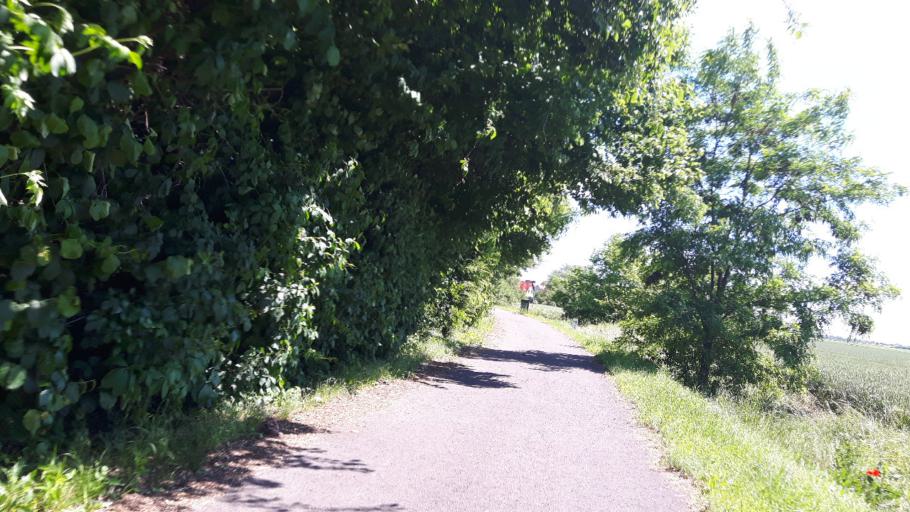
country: DE
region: Saxony-Anhalt
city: Lutzen
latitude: 51.2400
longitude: 12.1160
